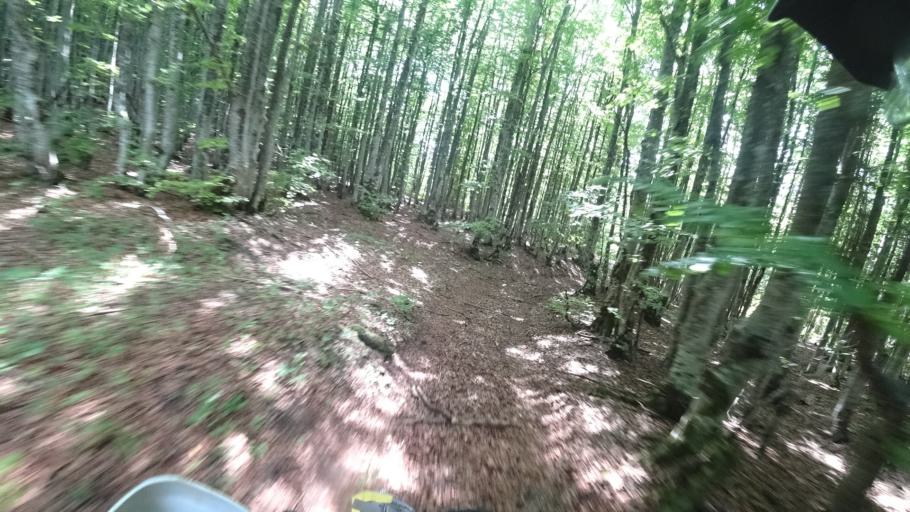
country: HR
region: Zadarska
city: Gracac
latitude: 44.4277
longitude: 15.9998
